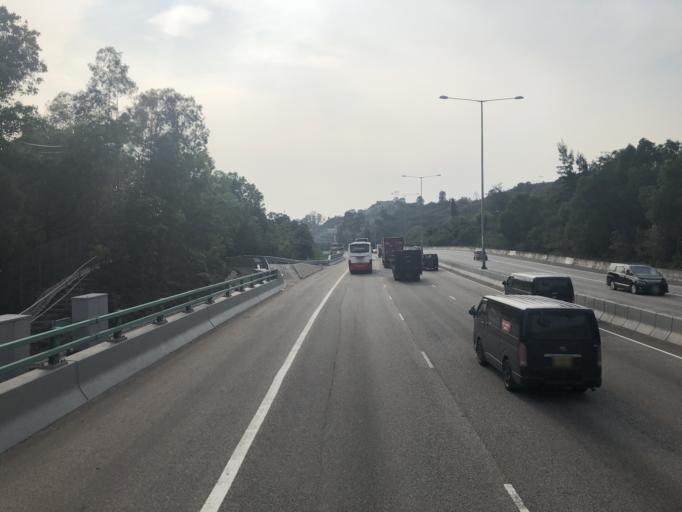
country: HK
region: Tuen Mun
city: Tuen Mun
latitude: 22.3668
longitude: 114.0083
